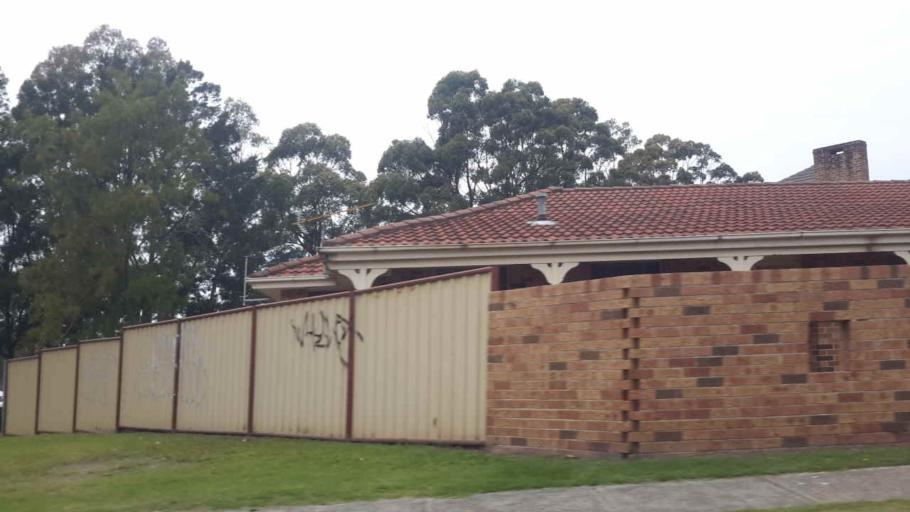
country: AU
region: New South Wales
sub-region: Wollongong
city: Bulli
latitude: -34.3511
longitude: 150.9027
